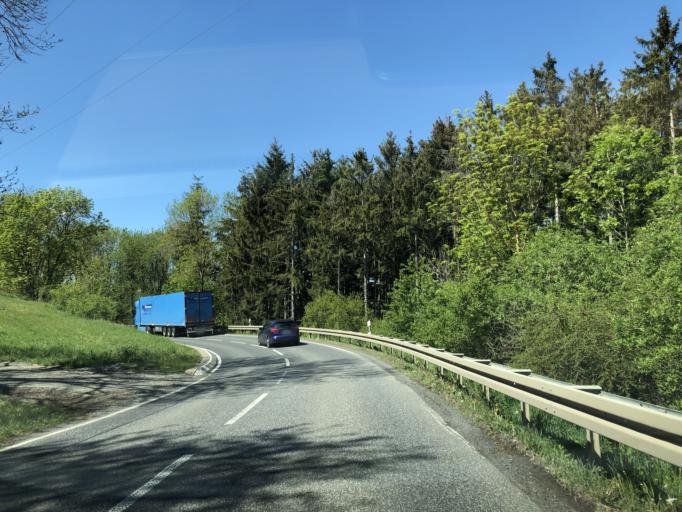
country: DE
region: Hesse
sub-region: Regierungsbezirk Kassel
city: Homberg
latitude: 51.0426
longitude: 9.4193
